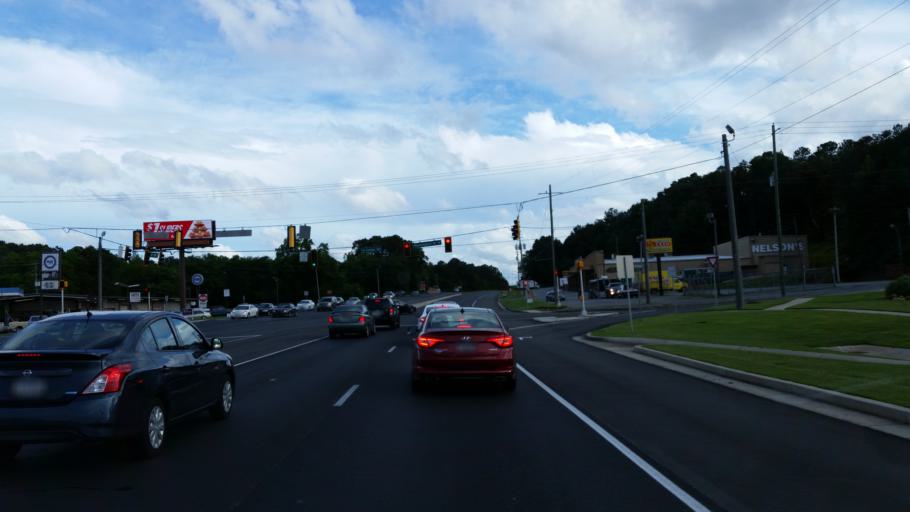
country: US
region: Georgia
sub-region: Bartow County
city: Cartersville
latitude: 34.1835
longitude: -84.7857
